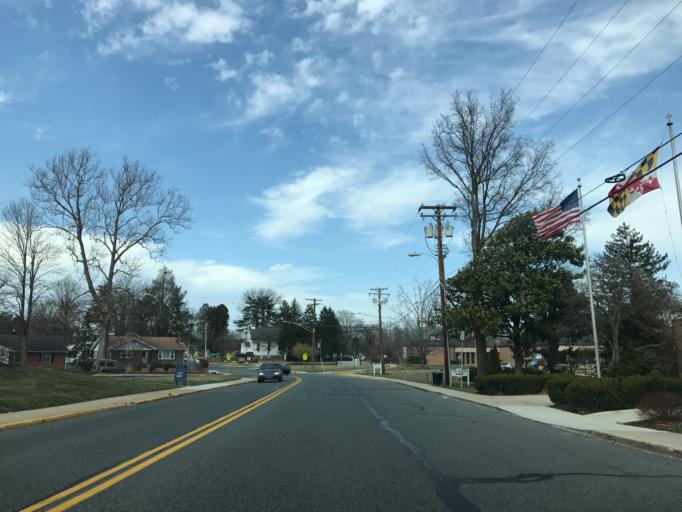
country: US
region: Maryland
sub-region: Harford County
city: Bel Air
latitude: 39.5386
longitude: -76.3484
